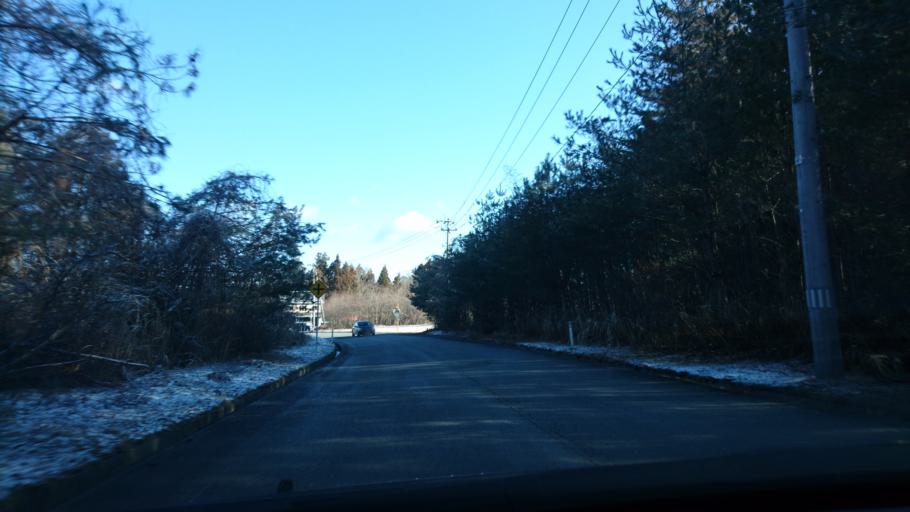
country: JP
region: Iwate
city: Ichinoseki
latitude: 38.8825
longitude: 141.3363
